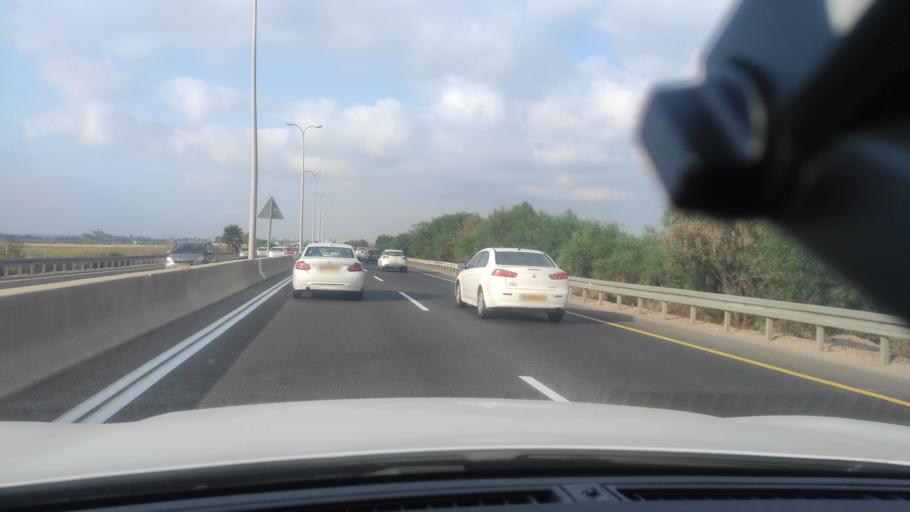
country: IL
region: Central District
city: Hod HaSharon
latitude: 32.1492
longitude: 34.9199
